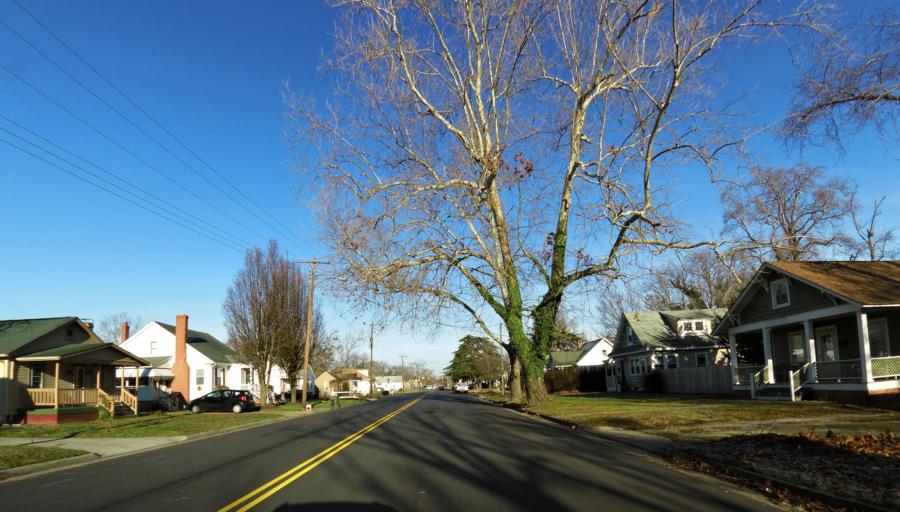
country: US
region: Virginia
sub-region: City of Hampton
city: Hampton
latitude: 37.0051
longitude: -76.3776
